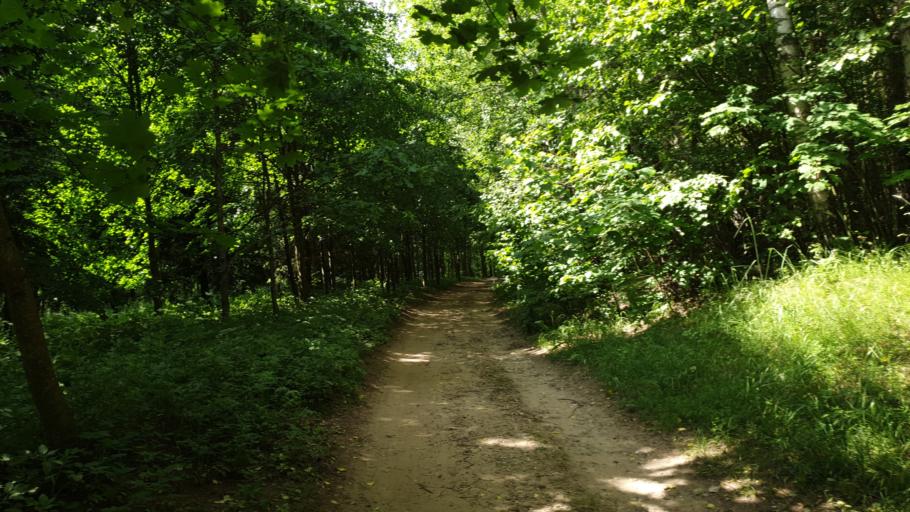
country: LT
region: Vilnius County
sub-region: Vilnius
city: Fabijoniskes
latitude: 54.7910
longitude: 25.3087
